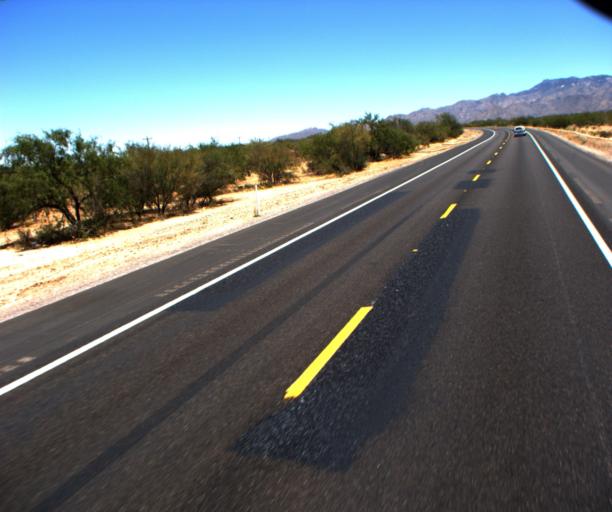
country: US
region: Arizona
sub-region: Pima County
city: Sells
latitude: 31.9289
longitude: -111.7878
